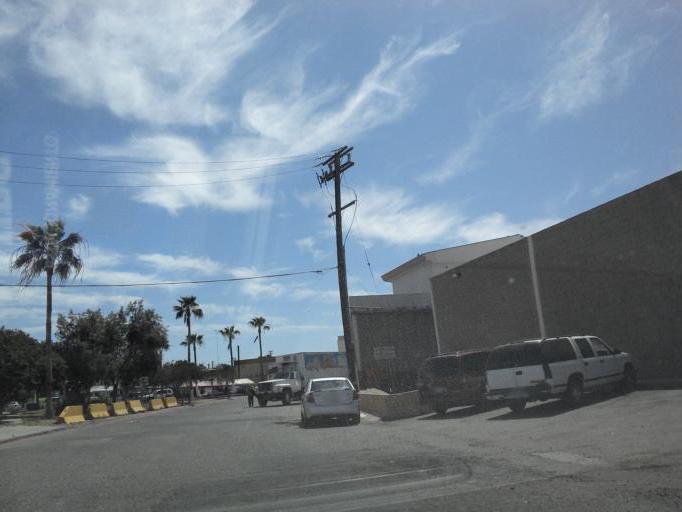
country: US
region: California
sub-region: San Diego County
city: Imperial Beach
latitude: 32.5325
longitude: -117.1121
